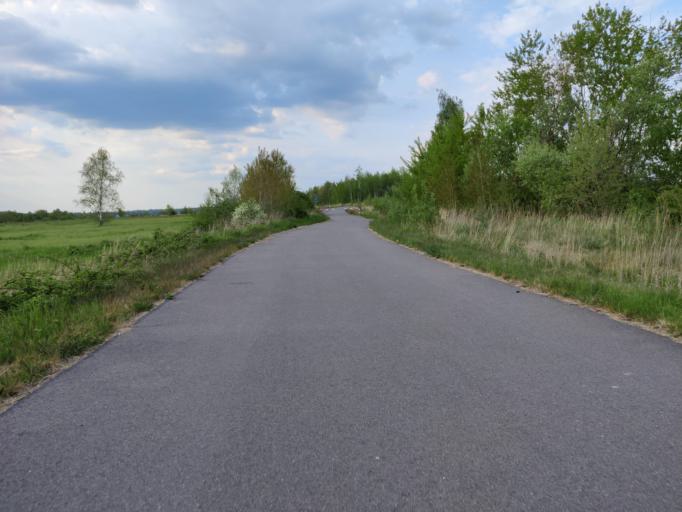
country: DE
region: Saxony
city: Rotha
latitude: 51.2209
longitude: 12.4477
